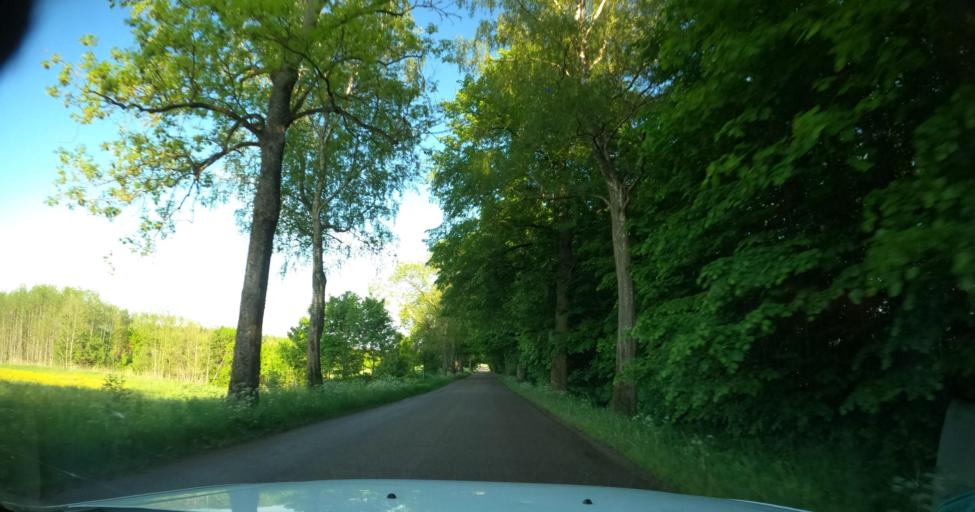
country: PL
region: Warmian-Masurian Voivodeship
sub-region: Powiat braniewski
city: Braniewo
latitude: 54.2766
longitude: 19.9229
